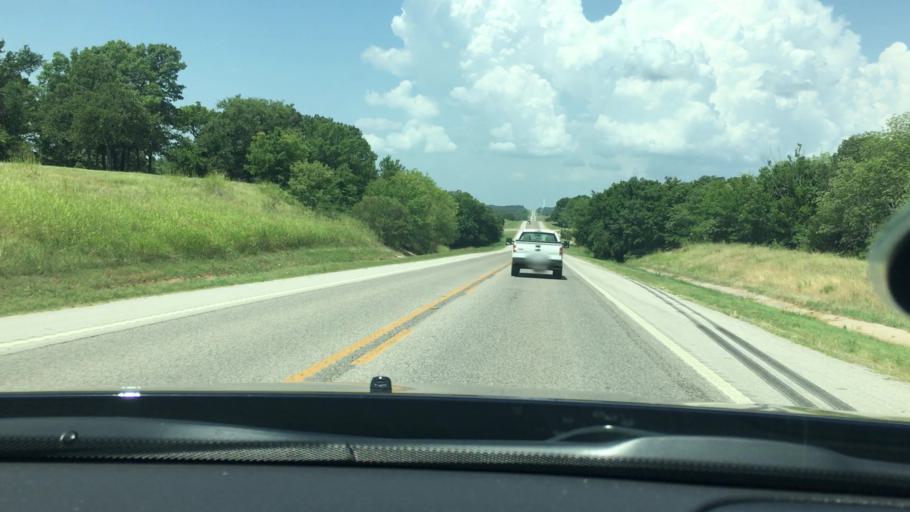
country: US
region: Oklahoma
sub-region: Marshall County
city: Oakland
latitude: 34.1002
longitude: -96.9054
